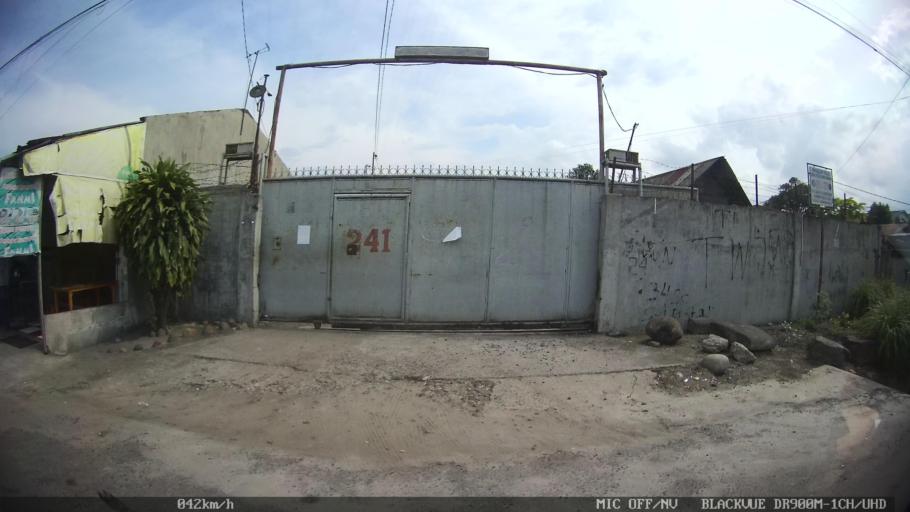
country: ID
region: North Sumatra
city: Percut
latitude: 3.6071
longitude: 98.7650
